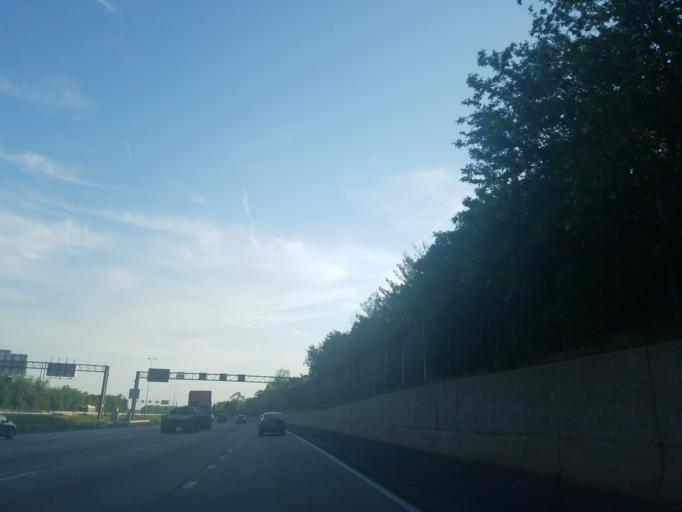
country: US
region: Virginia
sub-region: Fairfax County
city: Centreville
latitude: 38.8434
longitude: -77.4410
